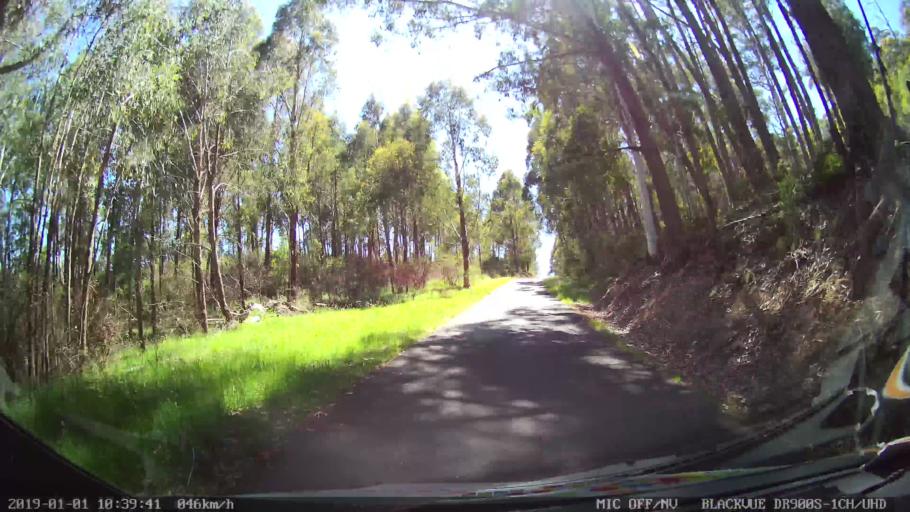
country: AU
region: New South Wales
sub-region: Snowy River
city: Jindabyne
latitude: -36.0396
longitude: 148.3066
